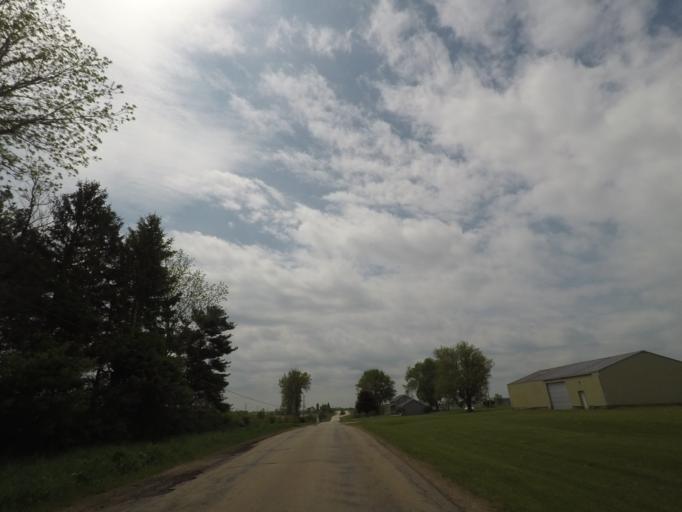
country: US
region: Illinois
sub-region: Winnebago County
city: Machesney Park
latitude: 42.3339
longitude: -88.9501
